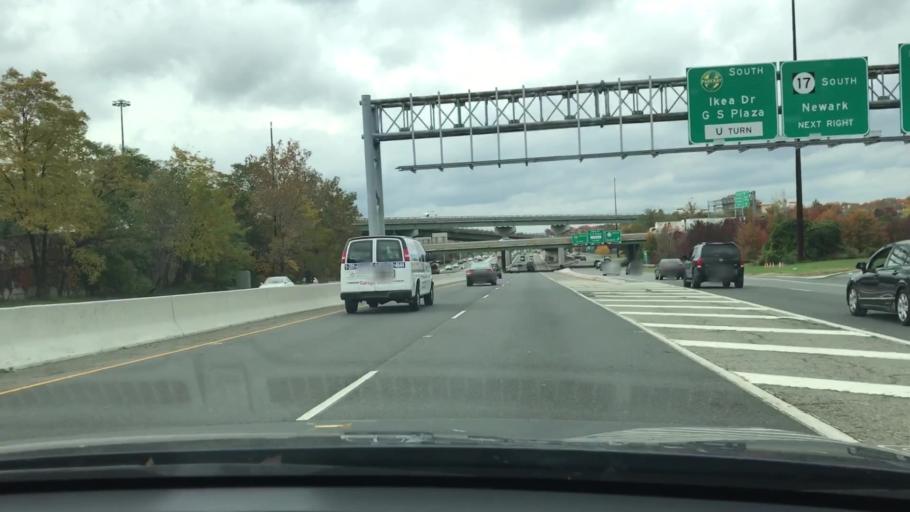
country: US
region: New Jersey
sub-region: Bergen County
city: Rochelle Park
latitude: 40.9202
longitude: -74.0699
